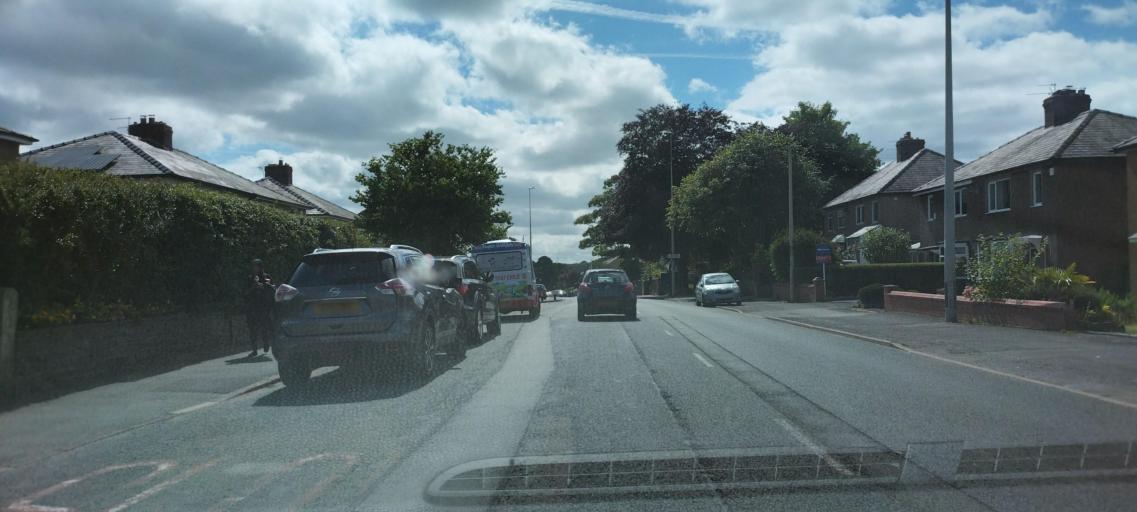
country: GB
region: England
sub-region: Blackburn with Darwen
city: Blackburn
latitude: 53.7299
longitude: -2.5260
